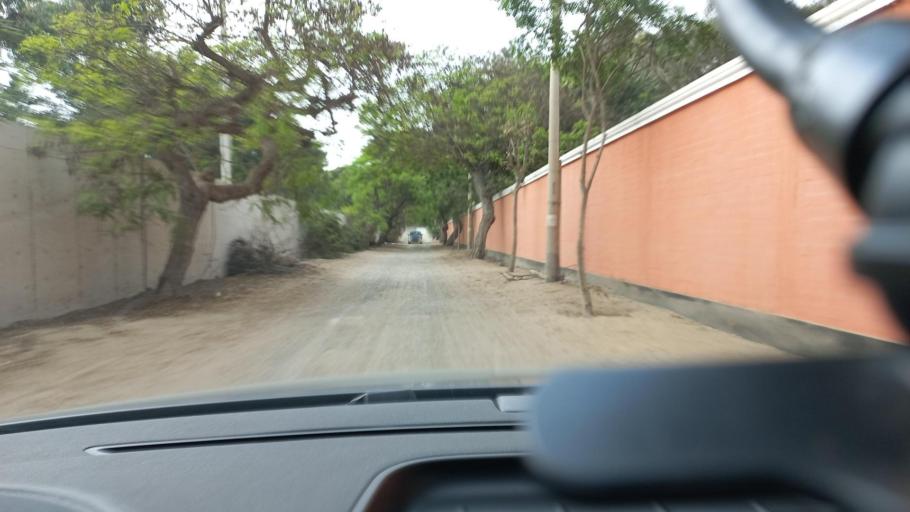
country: PE
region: Lima
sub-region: Lima
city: Punta Hermosa
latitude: -12.2611
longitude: -76.9088
